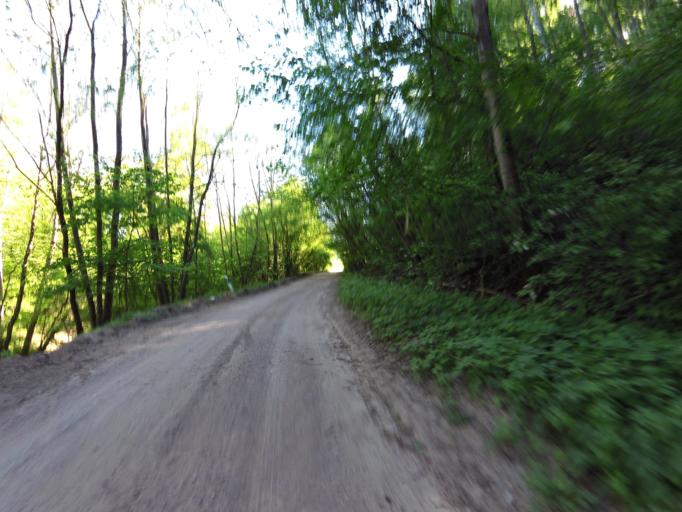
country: LT
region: Vilnius County
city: Pilaite
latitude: 54.6836
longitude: 25.1569
